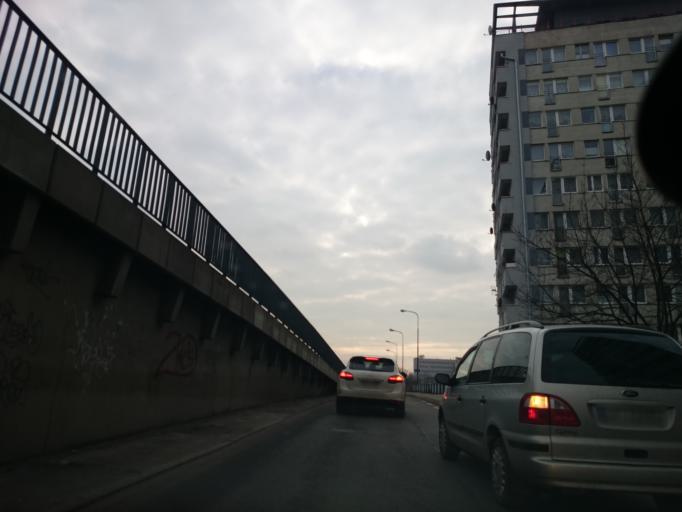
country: PL
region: Opole Voivodeship
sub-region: Powiat opolski
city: Opole
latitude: 50.6737
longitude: 17.9174
